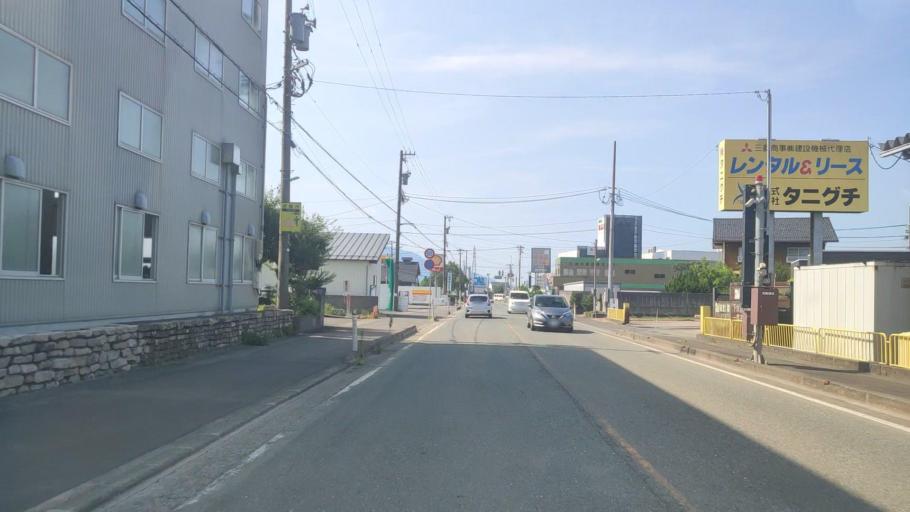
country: JP
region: Fukui
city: Tsuruga
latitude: 35.6278
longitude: 136.0736
